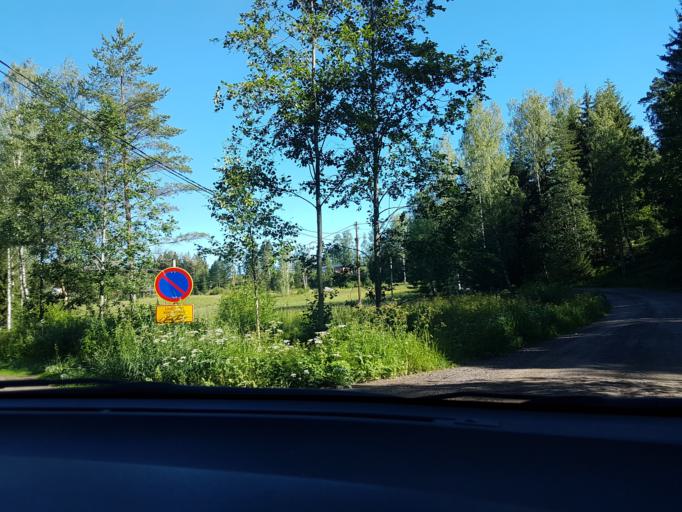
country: FI
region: Uusimaa
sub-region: Helsinki
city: Sibbo
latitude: 60.2920
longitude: 25.2409
